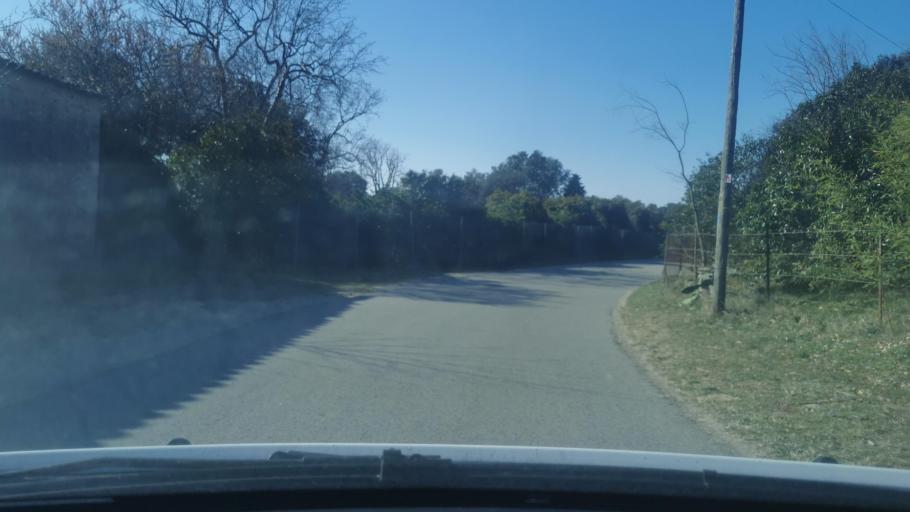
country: FR
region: Languedoc-Roussillon
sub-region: Departement du Gard
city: Montaren-et-Saint-Mediers
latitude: 44.0426
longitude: 4.3924
